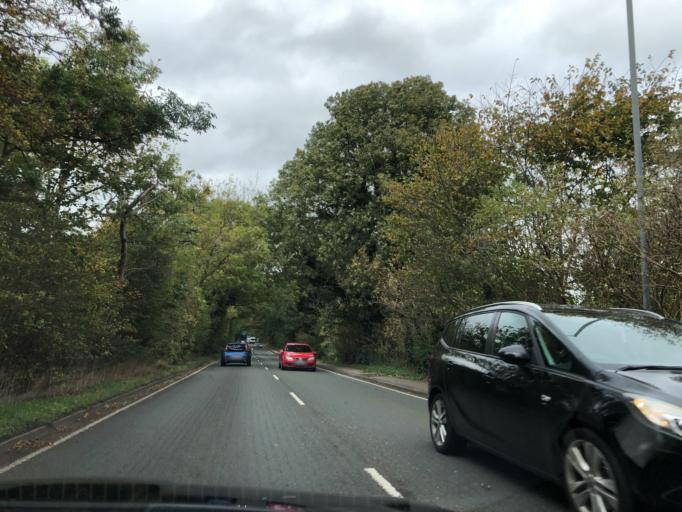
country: GB
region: England
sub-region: Warwickshire
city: Royal Leamington Spa
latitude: 52.3060
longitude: -1.5380
